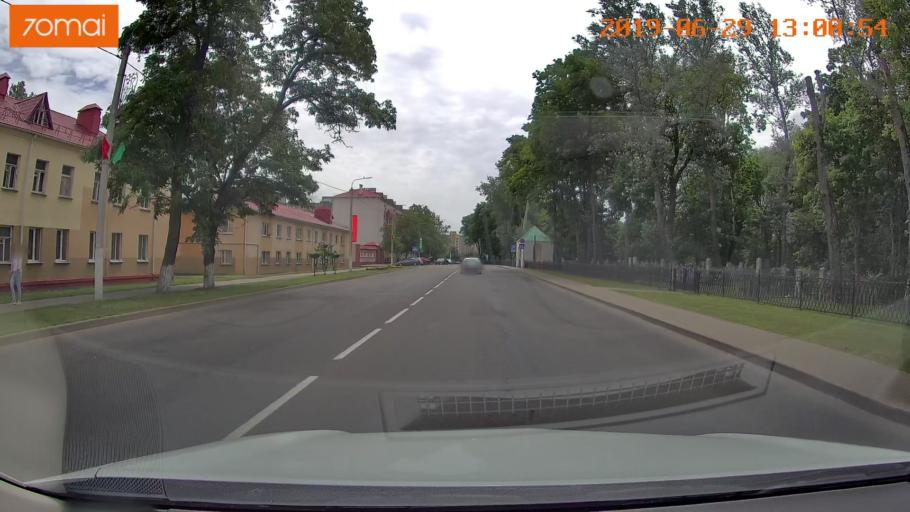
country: BY
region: Minsk
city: Slutsk
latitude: 53.0416
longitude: 27.5585
